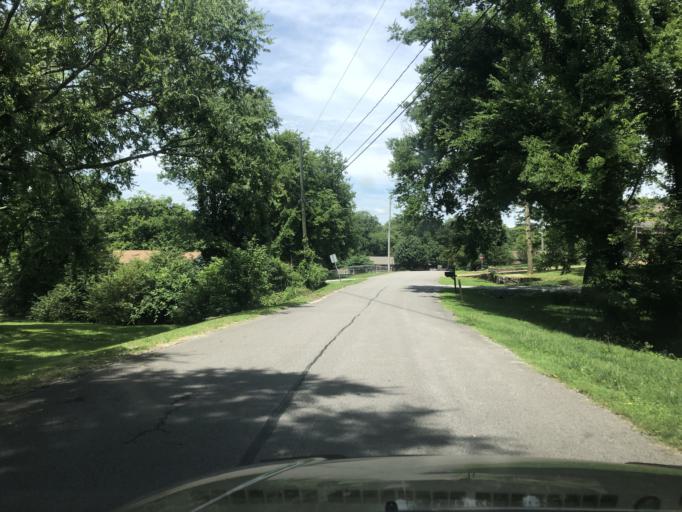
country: US
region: Tennessee
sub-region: Davidson County
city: Lakewood
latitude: 36.2482
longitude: -86.6883
